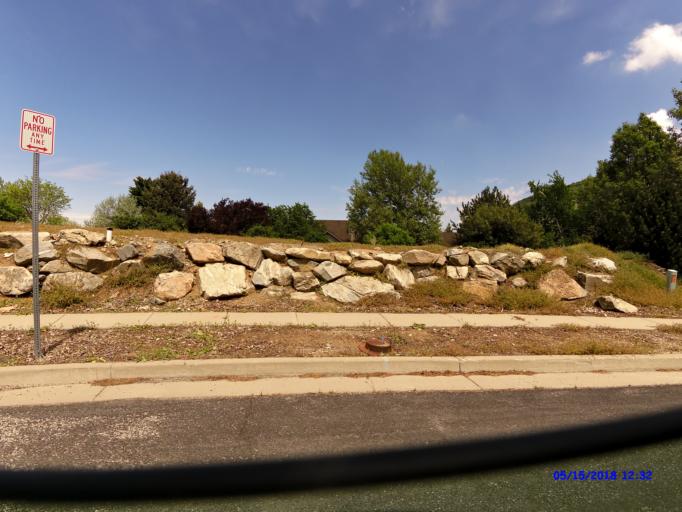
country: US
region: Utah
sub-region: Weber County
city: Uintah
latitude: 41.1756
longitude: -111.9334
